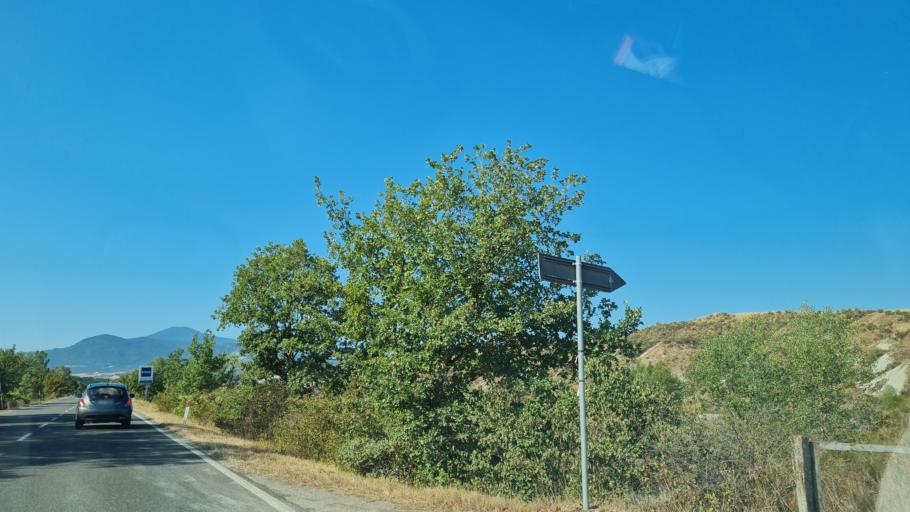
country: IT
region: Tuscany
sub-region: Provincia di Siena
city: Pienza
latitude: 43.0012
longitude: 11.7279
